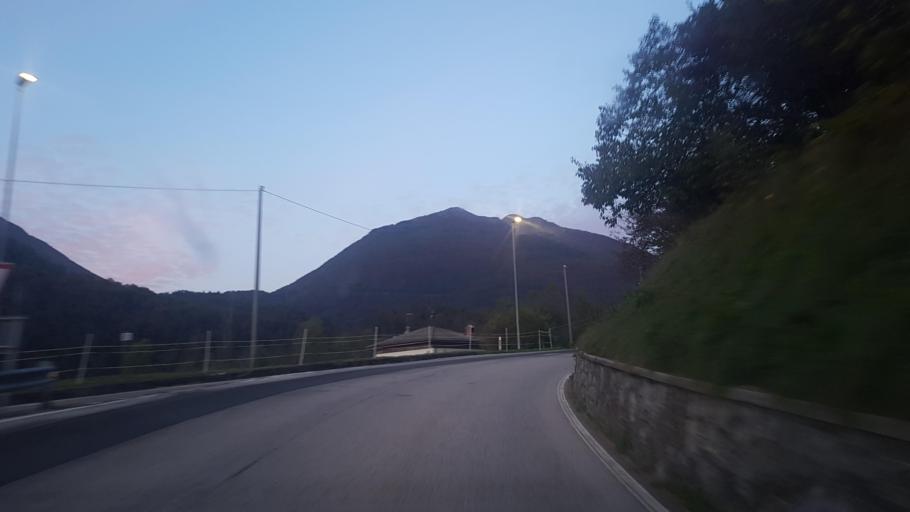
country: IT
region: Friuli Venezia Giulia
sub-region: Provincia di Udine
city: Chiaulis
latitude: 46.3827
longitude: 12.9904
